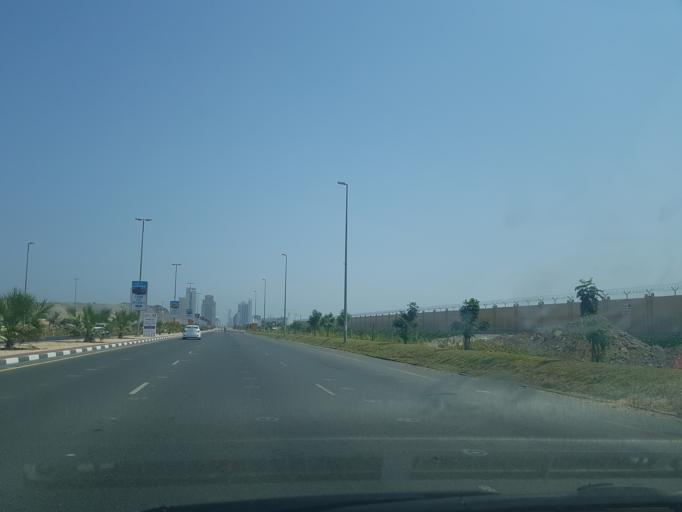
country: AE
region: Al Fujayrah
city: Al Fujayrah
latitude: 25.1225
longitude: 56.3033
